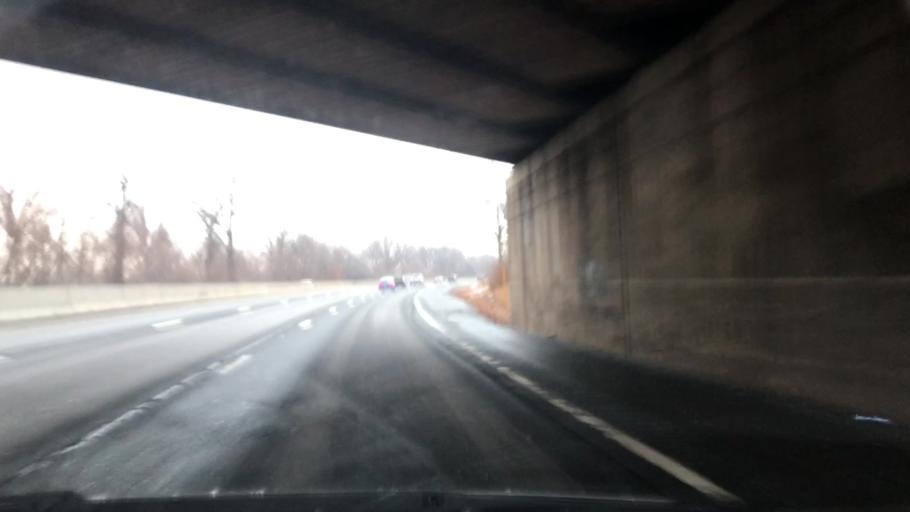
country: US
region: New Jersey
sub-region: Essex County
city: Bloomfield
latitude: 40.8167
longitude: -74.1794
